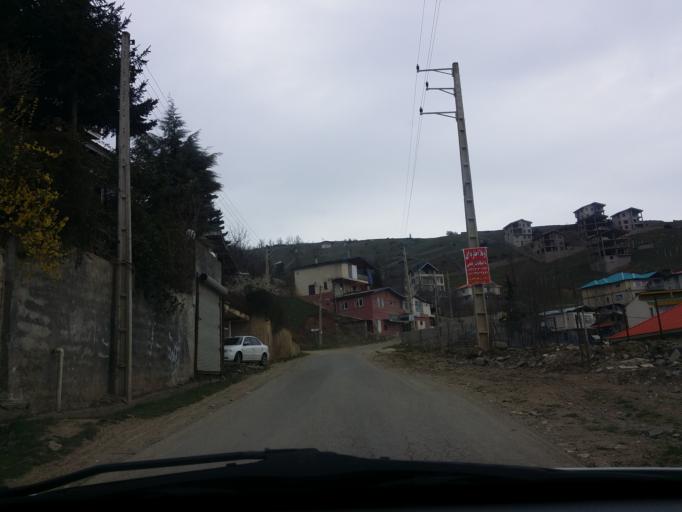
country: IR
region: Mazandaran
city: `Abbasabad
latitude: 36.5342
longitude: 51.1610
